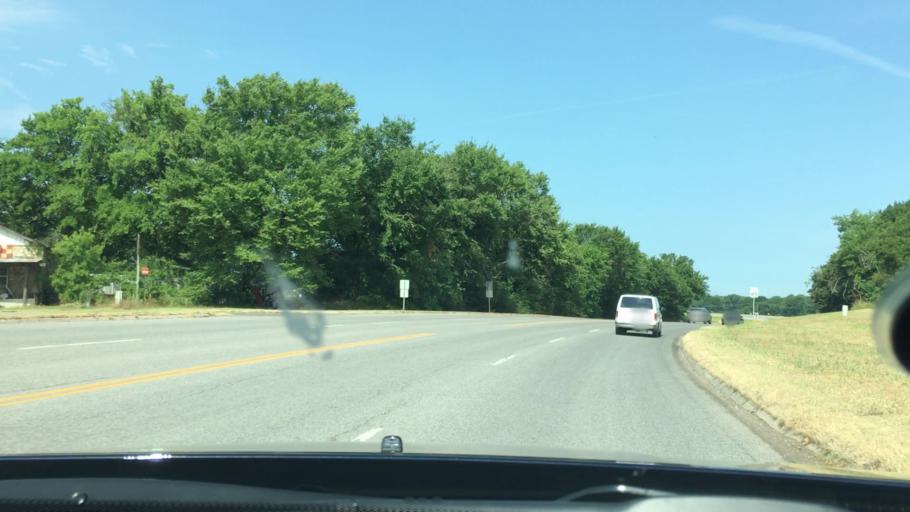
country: US
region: Oklahoma
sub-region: Murray County
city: Davis
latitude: 34.5024
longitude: -97.1272
